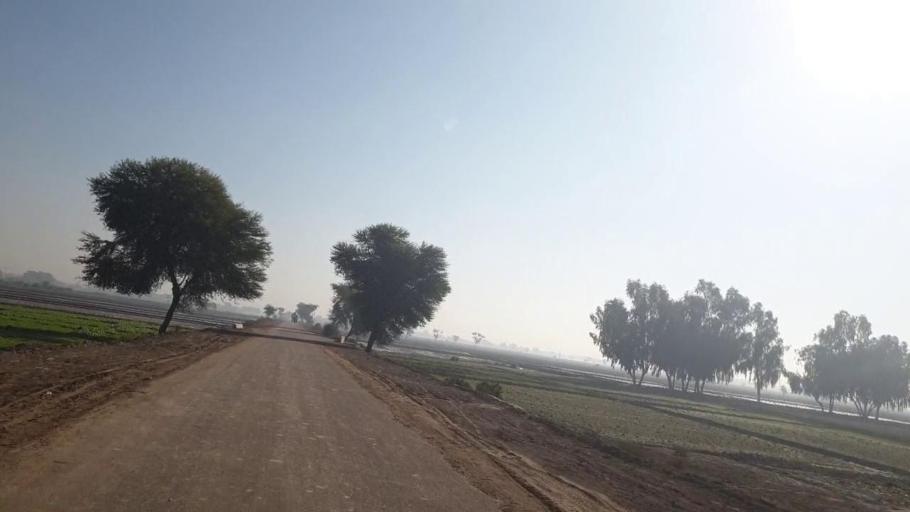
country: PK
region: Sindh
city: Dadu
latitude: 26.6712
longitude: 67.8393
